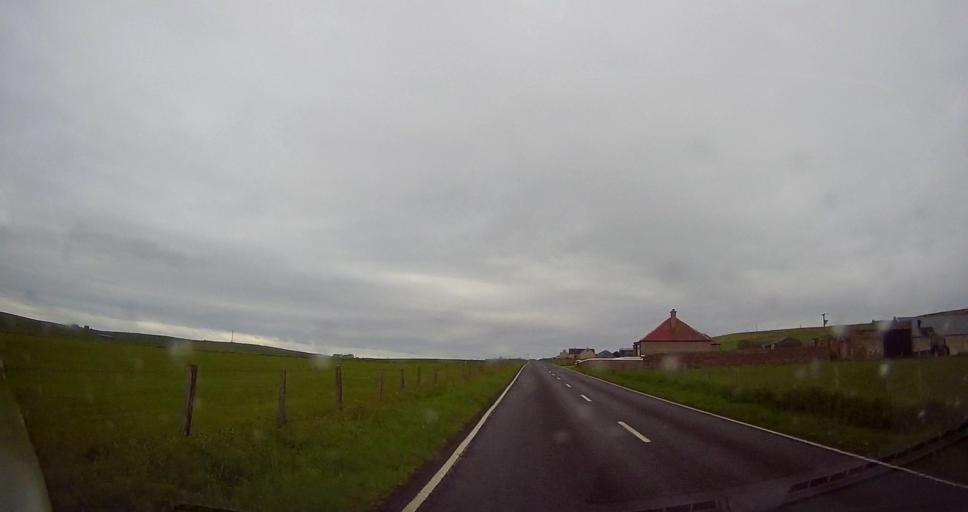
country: GB
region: Scotland
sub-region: Orkney Islands
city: Stromness
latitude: 58.9897
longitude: -3.2899
